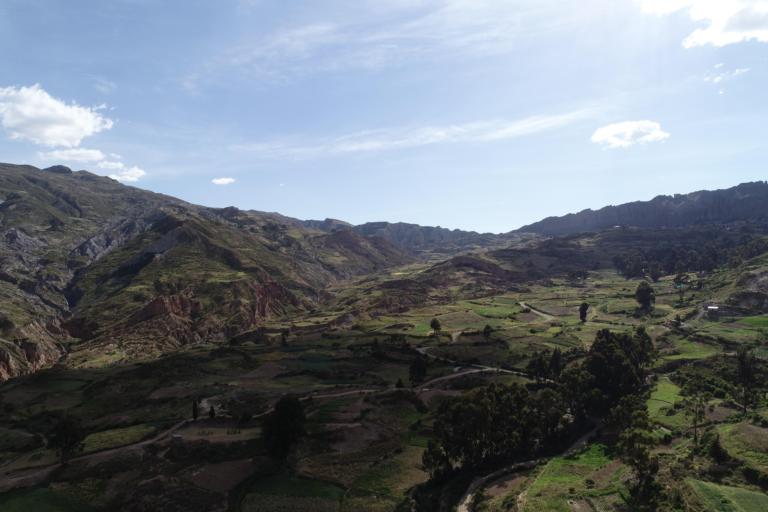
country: BO
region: La Paz
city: La Paz
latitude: -16.5552
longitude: -67.9844
